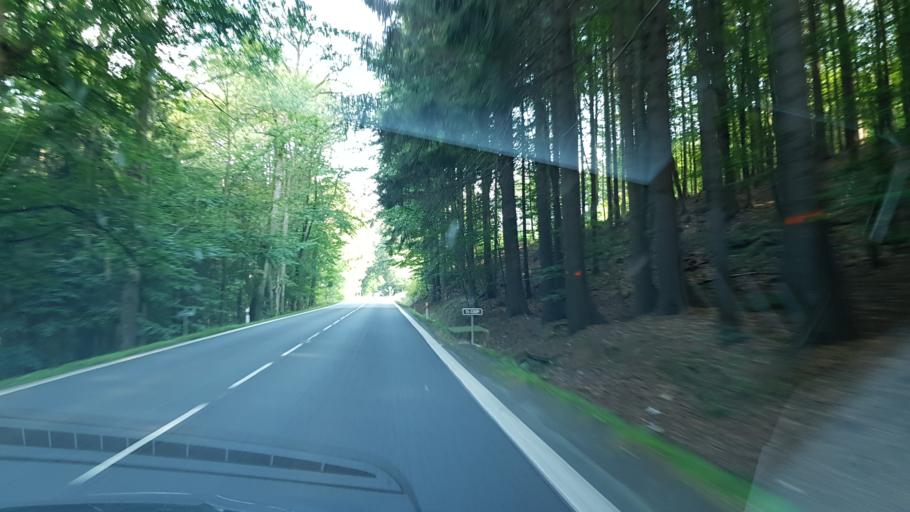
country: CZ
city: Vamberk
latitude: 50.1221
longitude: 16.3419
